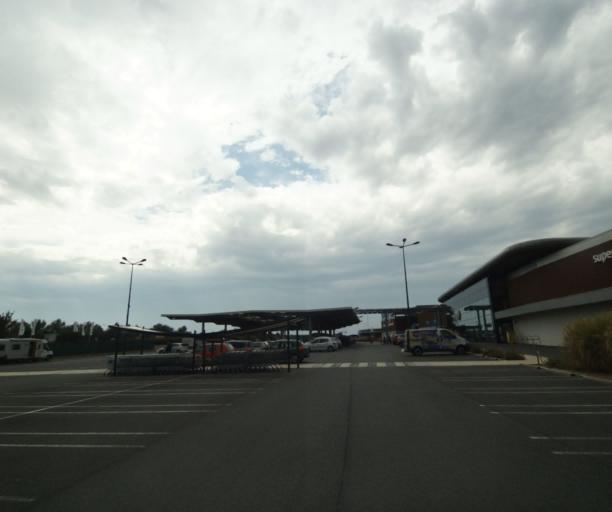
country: FR
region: Poitou-Charentes
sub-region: Departement de la Charente-Maritime
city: Tonnay-Charente
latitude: 45.9513
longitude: -0.8971
